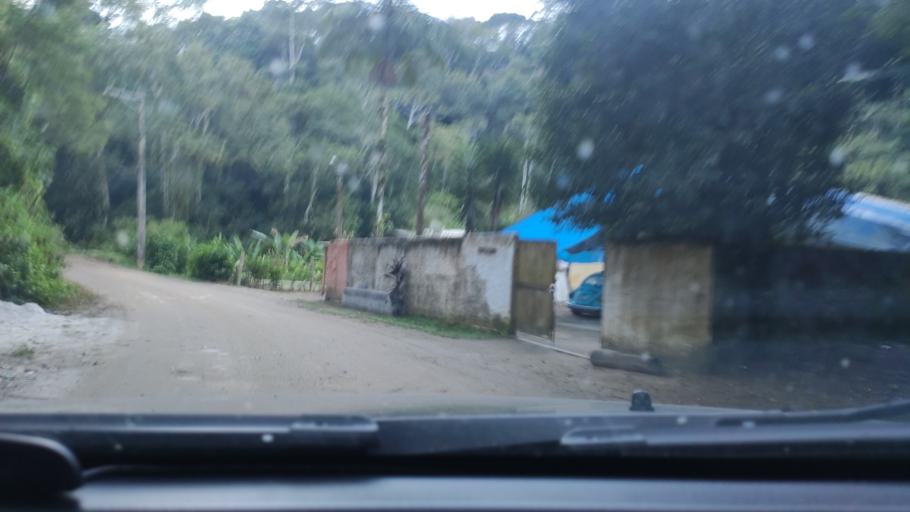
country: BR
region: Sao Paulo
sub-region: Sao Sebastiao
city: Sao Sebastiao
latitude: -23.7189
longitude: -45.4940
